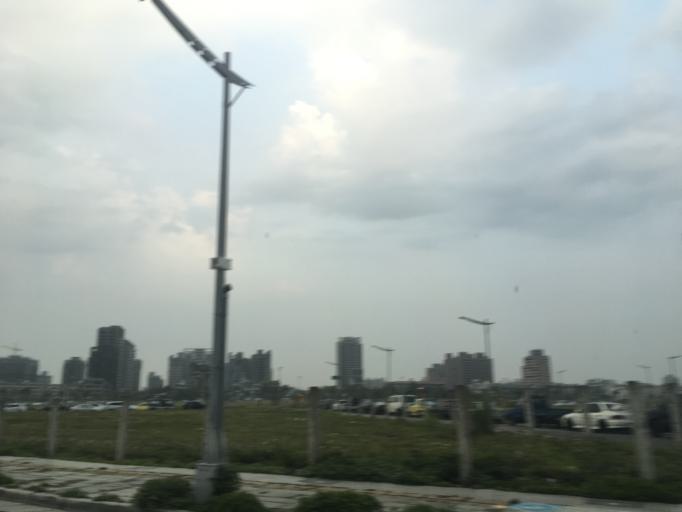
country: TW
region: Taiwan
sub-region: Taichung City
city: Taichung
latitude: 24.1860
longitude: 120.6956
